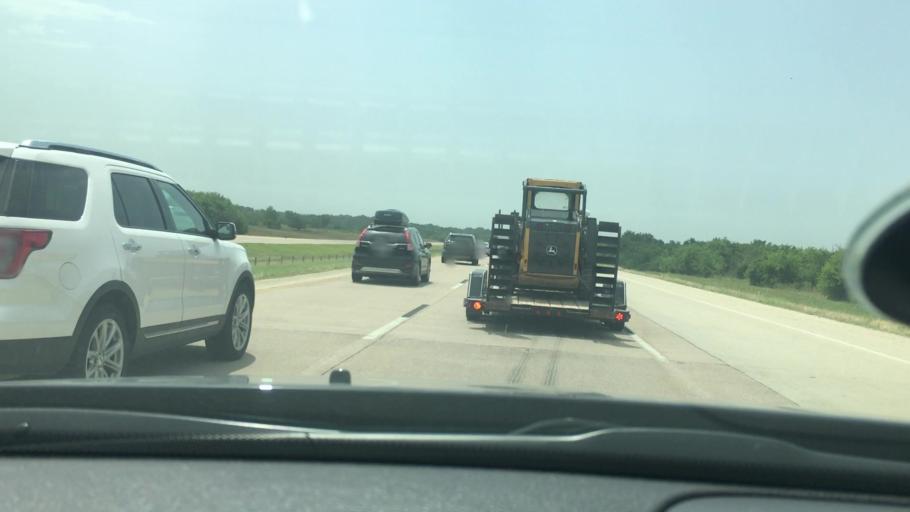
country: US
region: Oklahoma
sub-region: Garvin County
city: Pauls Valley
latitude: 34.7024
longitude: -97.2424
